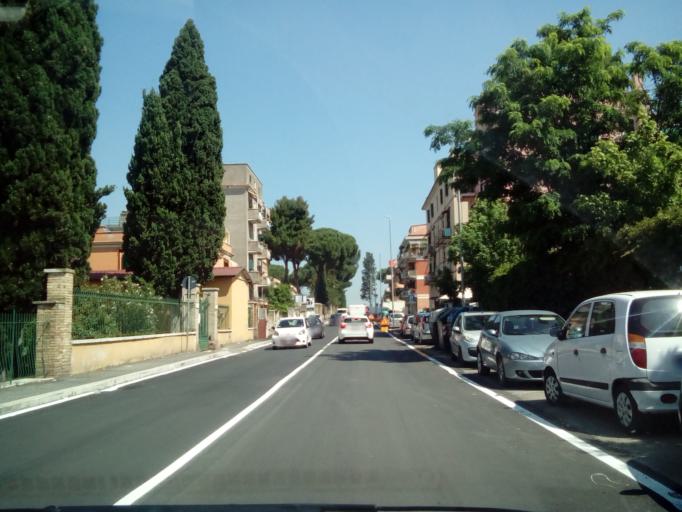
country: IT
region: Latium
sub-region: Citta metropolitana di Roma Capitale
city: Rome
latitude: 41.8852
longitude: 12.5769
